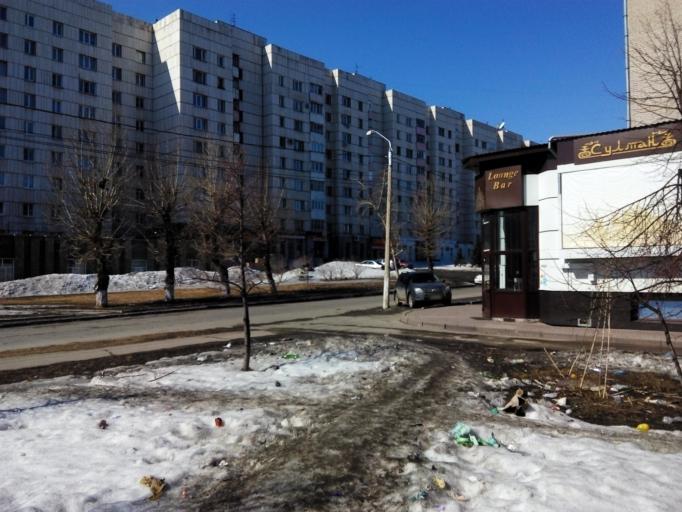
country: RU
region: Altai Krai
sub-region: Gorod Barnaulskiy
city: Barnaul
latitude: 53.3406
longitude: 83.7797
